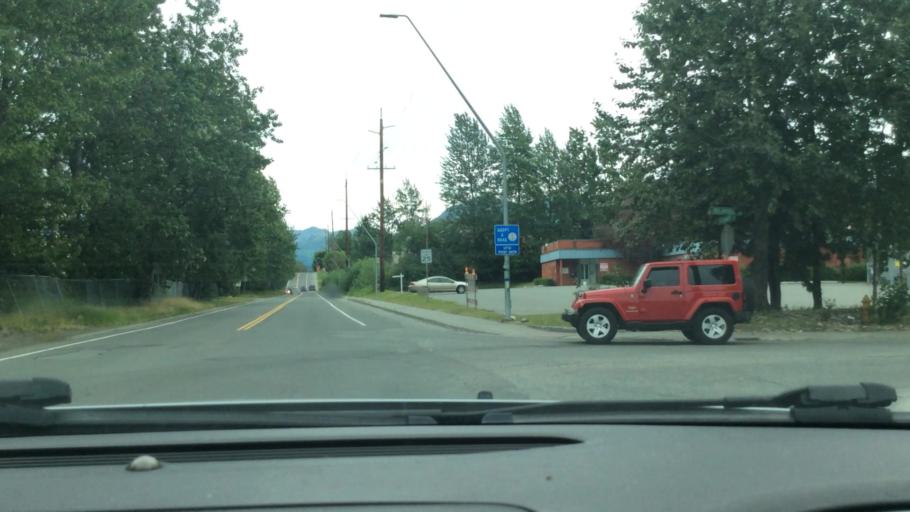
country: US
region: Alaska
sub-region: Anchorage Municipality
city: Elmendorf Air Force Base
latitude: 61.2242
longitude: -149.7451
